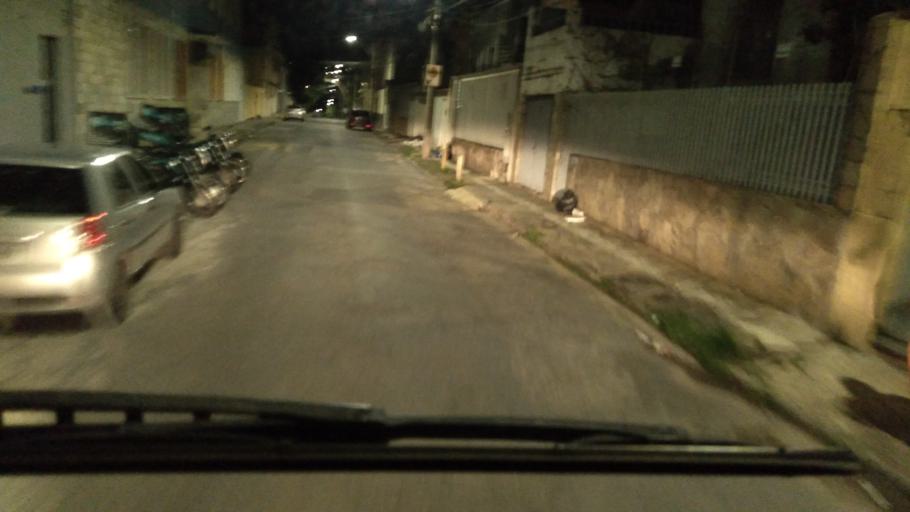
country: BR
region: Minas Gerais
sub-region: Belo Horizonte
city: Belo Horizonte
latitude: -19.9089
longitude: -43.9622
